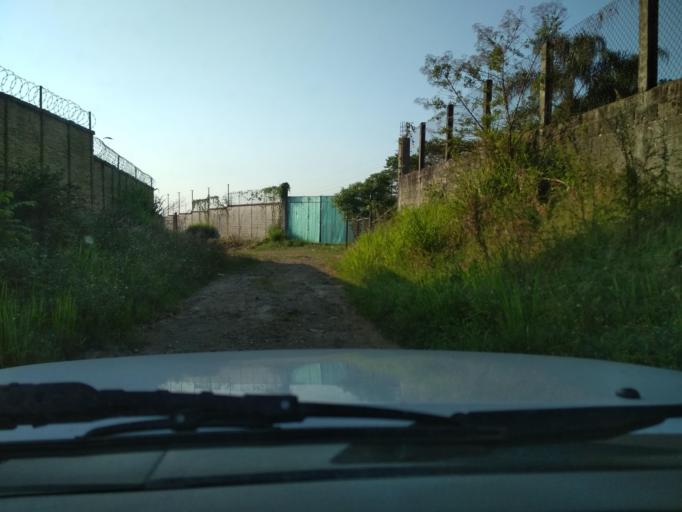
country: MX
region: Veracruz
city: Cordoba
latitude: 18.8678
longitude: -96.9323
